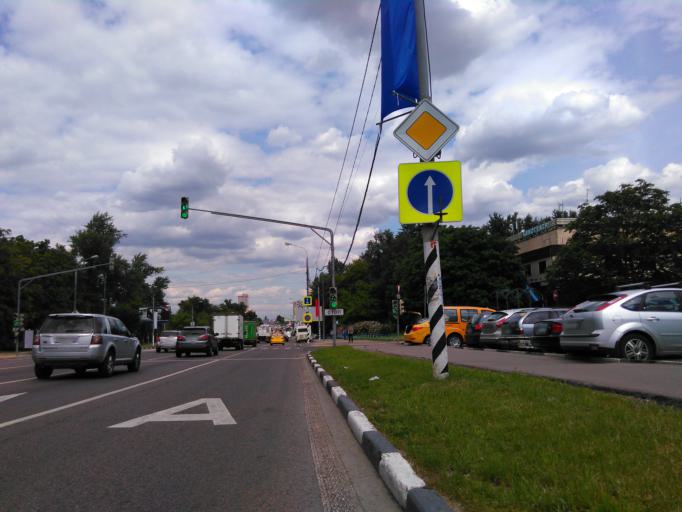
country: RU
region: Moscow
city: Kotlovka
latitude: 55.6748
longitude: 37.5909
